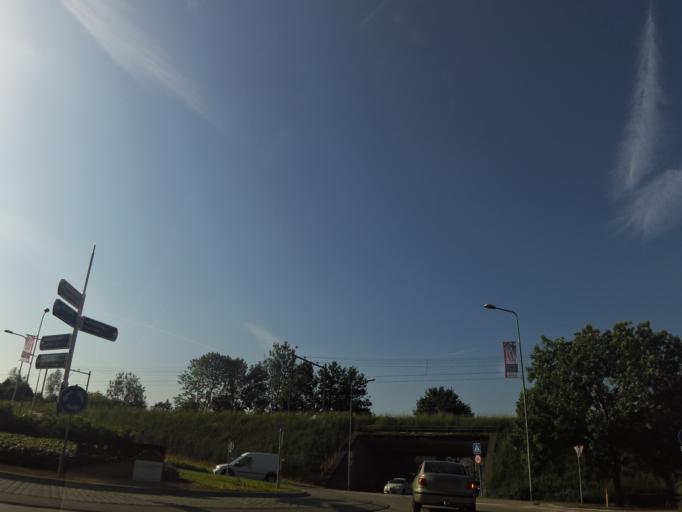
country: NL
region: Limburg
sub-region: Valkenburg aan de Geul
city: Broekhem
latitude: 50.8734
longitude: 5.8142
